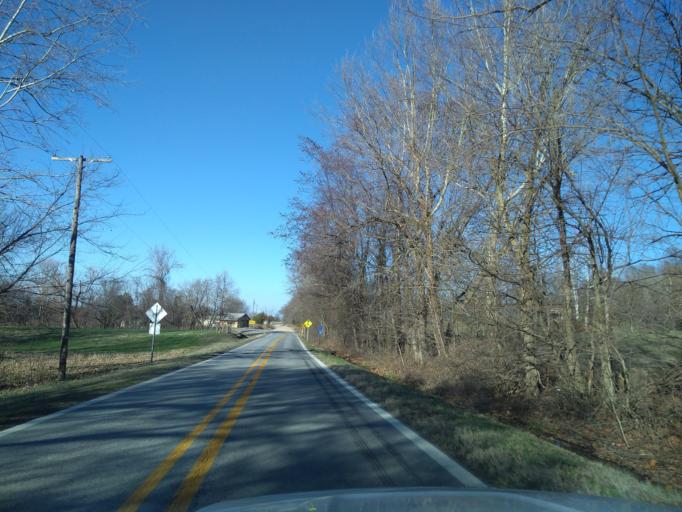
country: US
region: Arkansas
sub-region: Washington County
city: Lincoln
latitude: 35.9446
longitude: -94.3761
